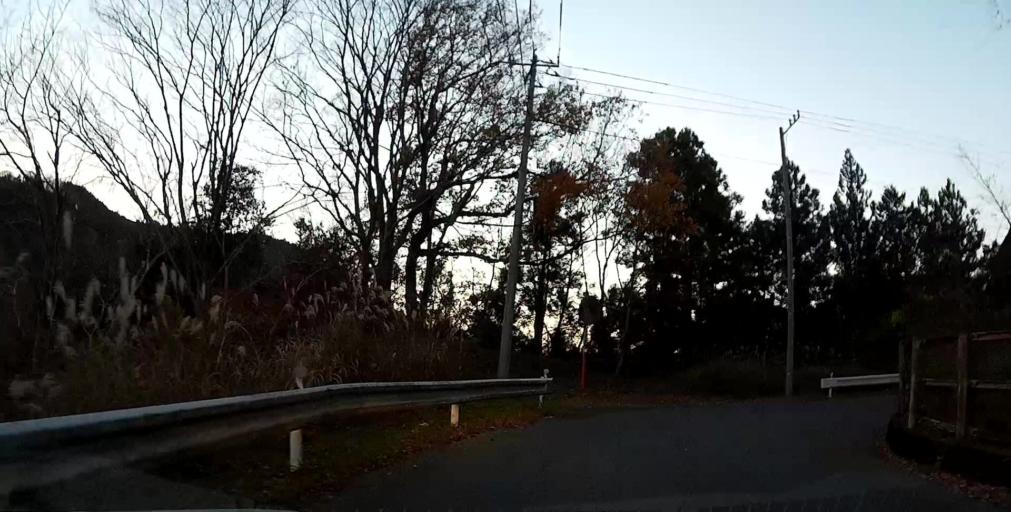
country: JP
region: Yamanashi
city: Uenohara
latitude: 35.5725
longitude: 139.1958
